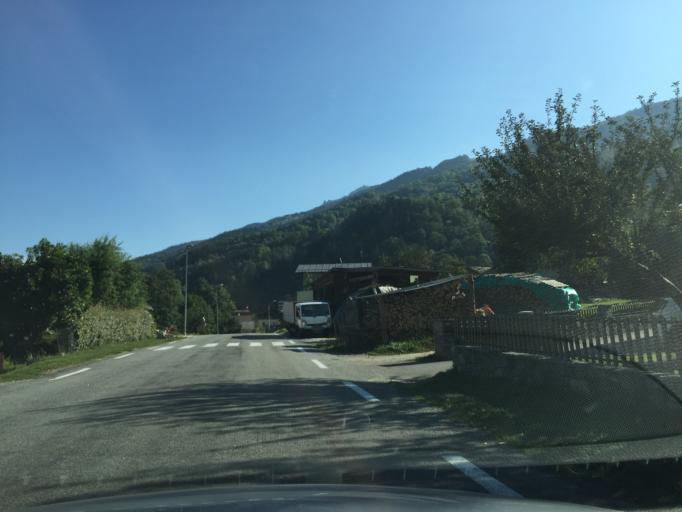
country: FR
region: Rhone-Alpes
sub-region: Departement de la Savoie
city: Bourg-Saint-Maurice
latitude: 45.5705
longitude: 6.7370
